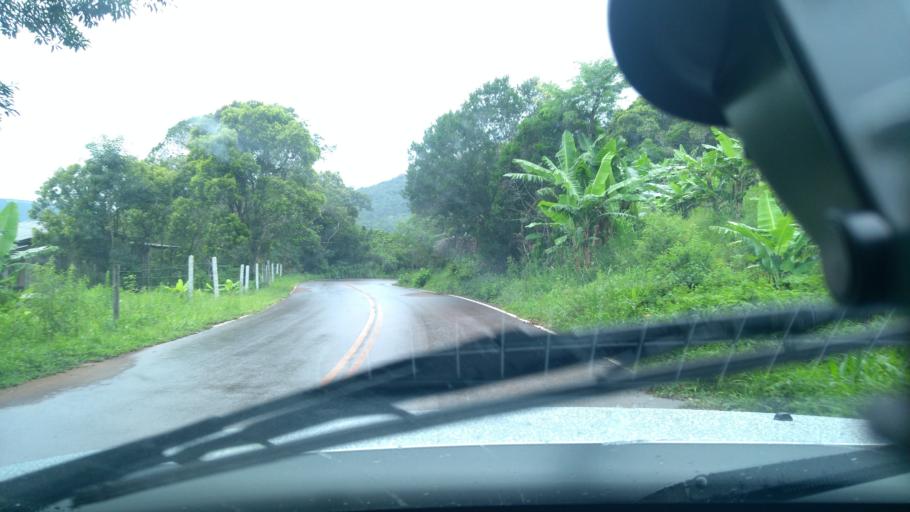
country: BR
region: Rio Grande do Sul
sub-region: Torres
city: Torres
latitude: -29.1823
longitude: -49.9863
